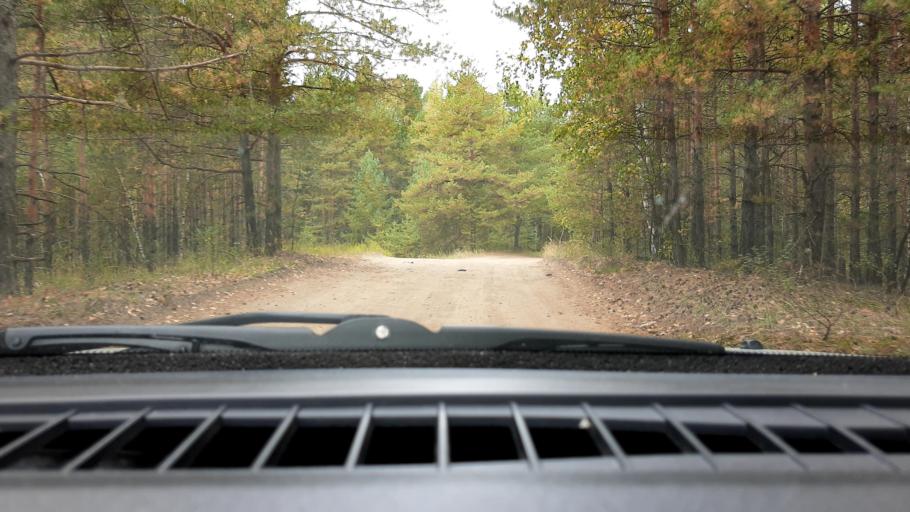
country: RU
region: Nizjnij Novgorod
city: Gorbatovka
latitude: 56.3201
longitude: 43.6930
